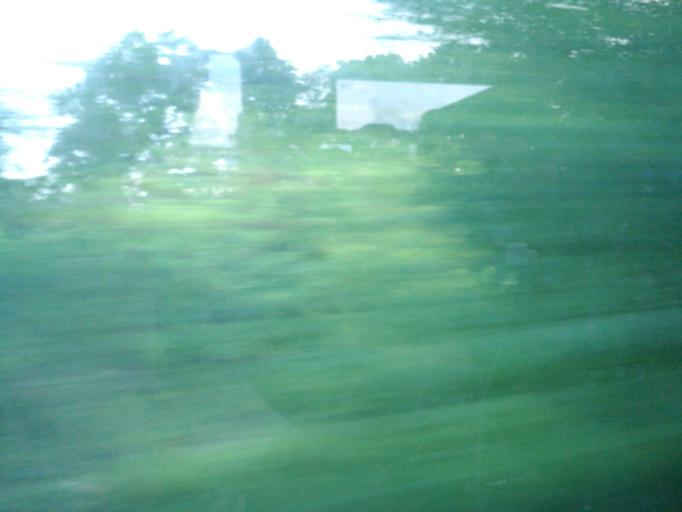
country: RO
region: Ilfov
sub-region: Comuna Buftea
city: Buciumeni
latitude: 44.5253
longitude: 25.9448
